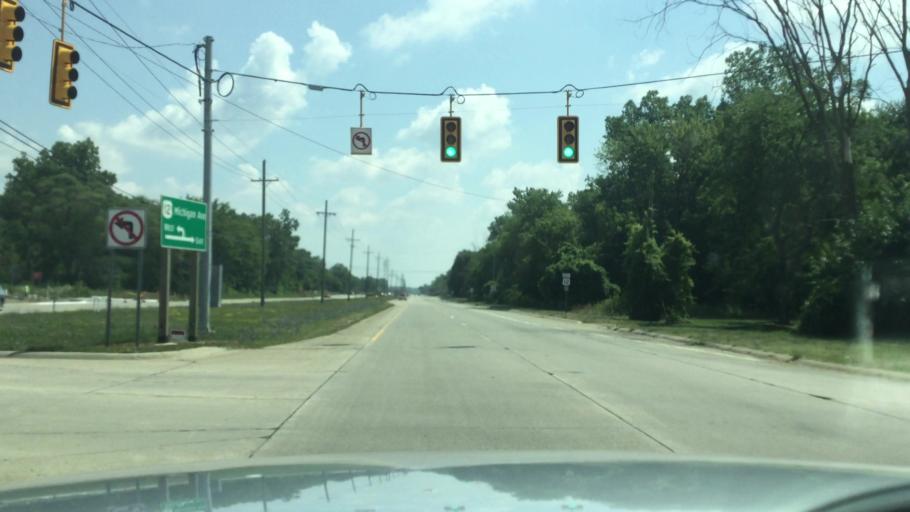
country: US
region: Michigan
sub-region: Wayne County
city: Canton
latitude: 42.2615
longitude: -83.5244
